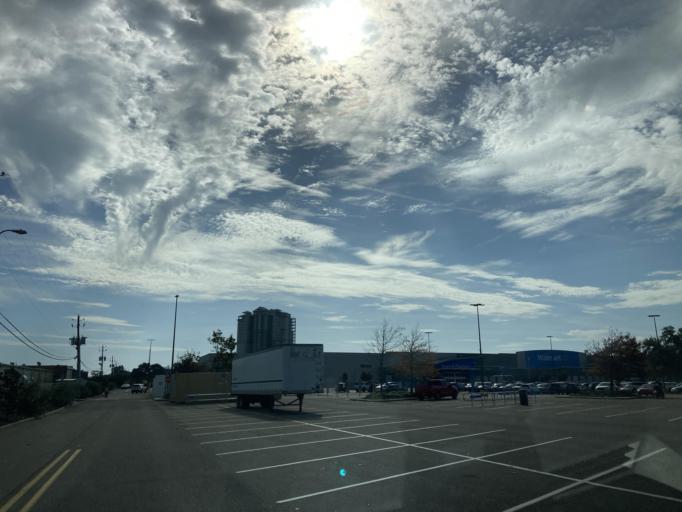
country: US
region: Mississippi
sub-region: Harrison County
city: West Gulfport
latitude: 30.3941
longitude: -88.9939
